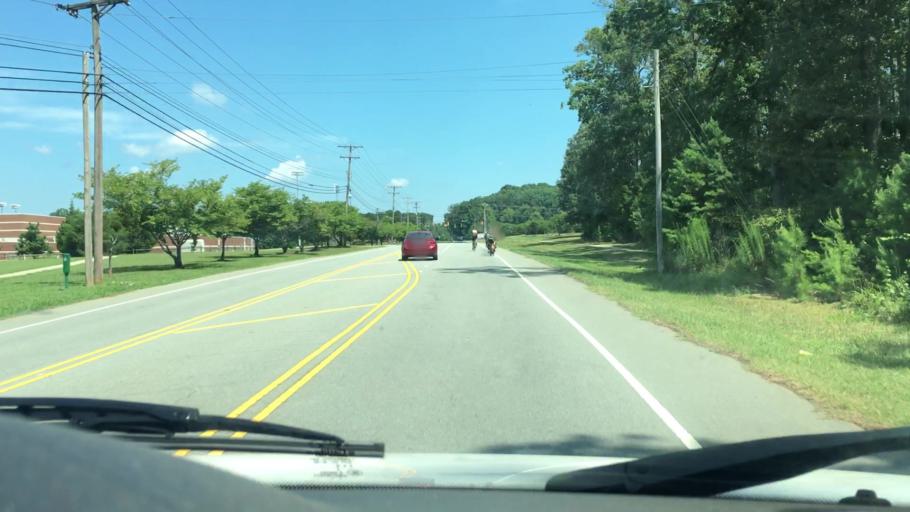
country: US
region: North Carolina
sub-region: Mecklenburg County
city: Huntersville
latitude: 35.3984
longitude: -80.9232
